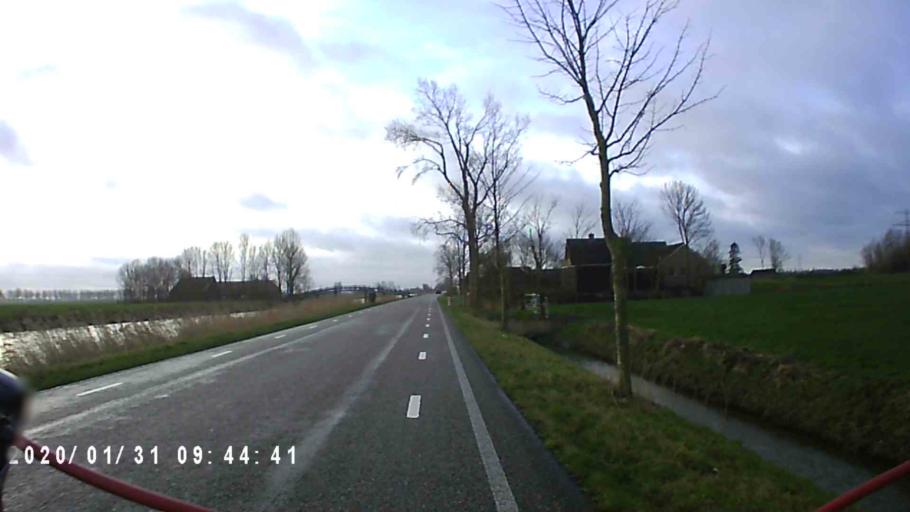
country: NL
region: Groningen
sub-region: Gemeente Zuidhorn
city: Aduard
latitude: 53.2716
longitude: 6.4838
